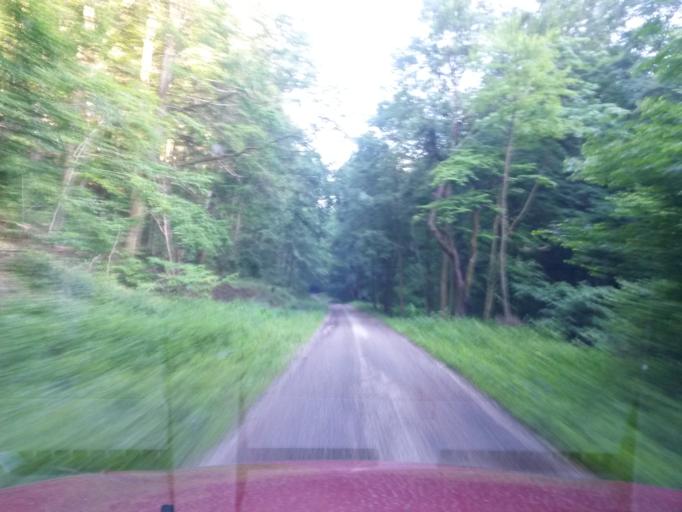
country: SK
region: Kosicky
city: Moldava nad Bodvou
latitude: 48.7369
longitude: 21.0644
